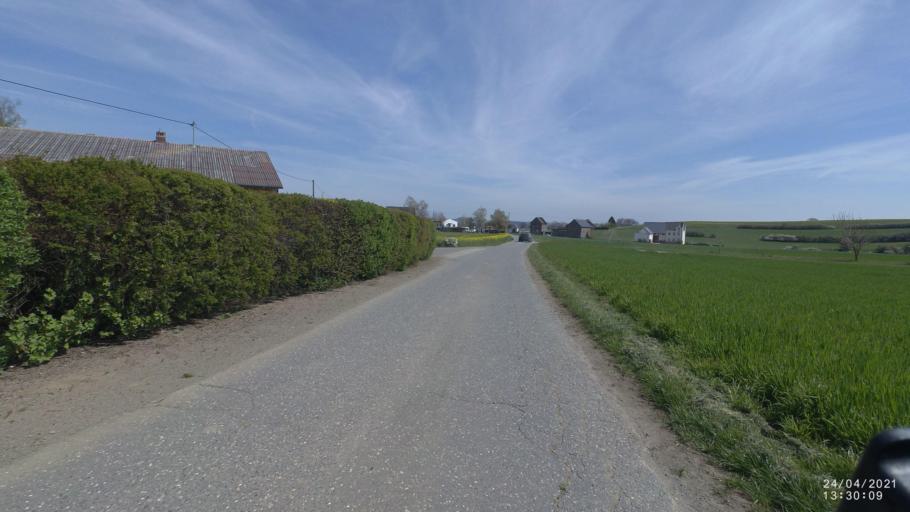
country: DE
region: Rheinland-Pfalz
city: Trimbs
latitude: 50.3322
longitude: 7.3009
